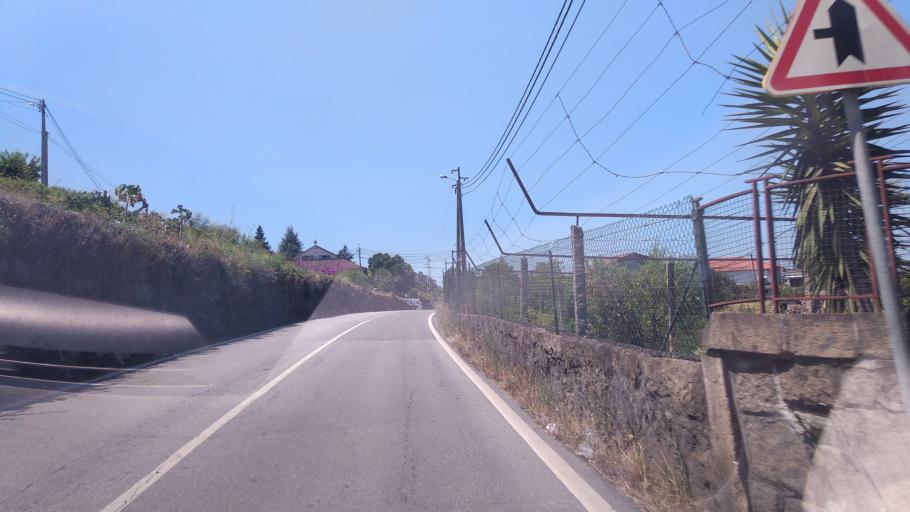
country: PT
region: Braga
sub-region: Braga
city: Adaufe
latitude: 41.5814
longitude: -8.4061
